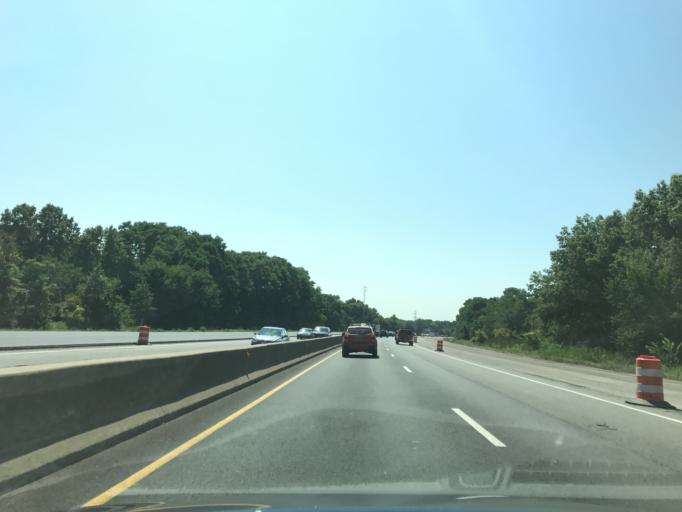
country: US
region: Indiana
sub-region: Porter County
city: Porter
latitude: 41.6116
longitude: -87.0898
